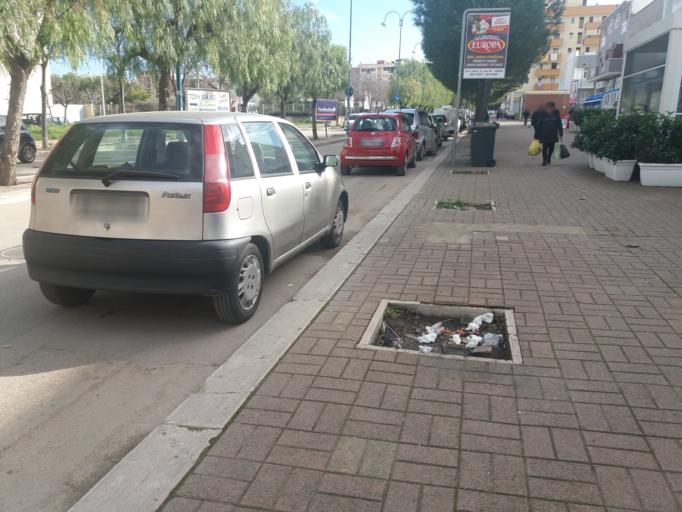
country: IT
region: Apulia
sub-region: Provincia di Barletta - Andria - Trani
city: Andria
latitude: 41.2351
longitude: 16.2980
